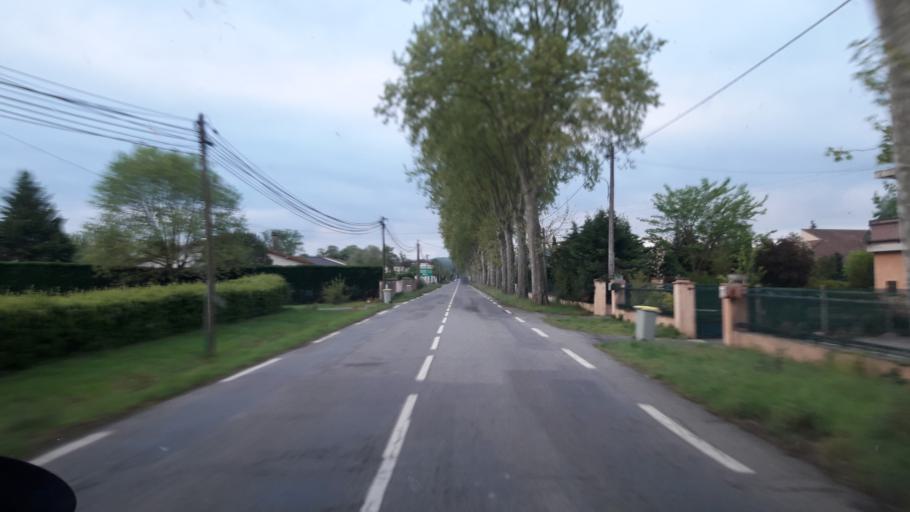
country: FR
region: Midi-Pyrenees
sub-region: Departement de la Haute-Garonne
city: Cazeres
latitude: 43.2232
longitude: 1.0848
